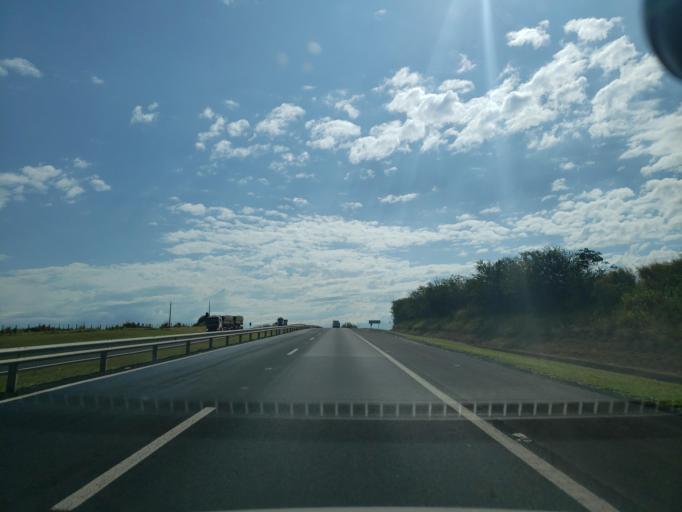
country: BR
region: Sao Paulo
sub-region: Pirajui
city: Pirajui
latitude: -22.0218
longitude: -49.4106
